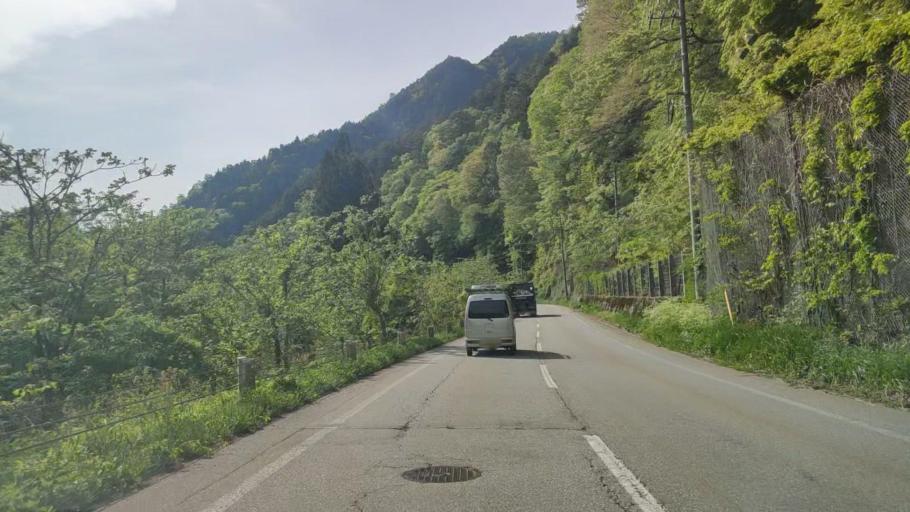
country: JP
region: Gifu
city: Takayama
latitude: 36.2580
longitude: 137.4683
